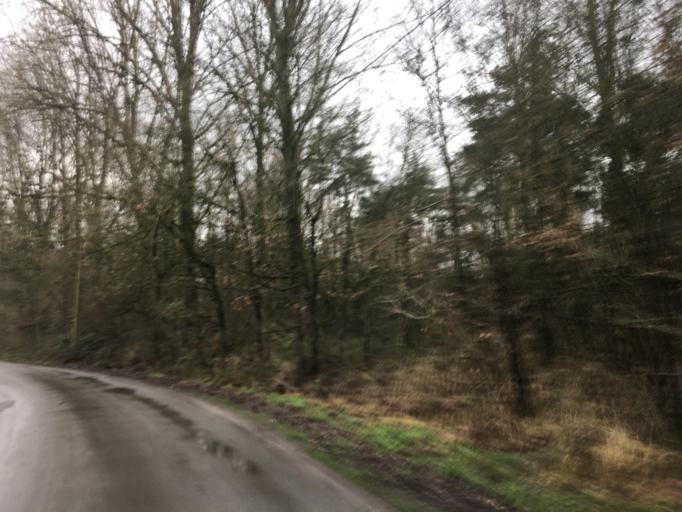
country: DE
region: North Rhine-Westphalia
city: Olfen
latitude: 51.7692
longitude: 7.3347
